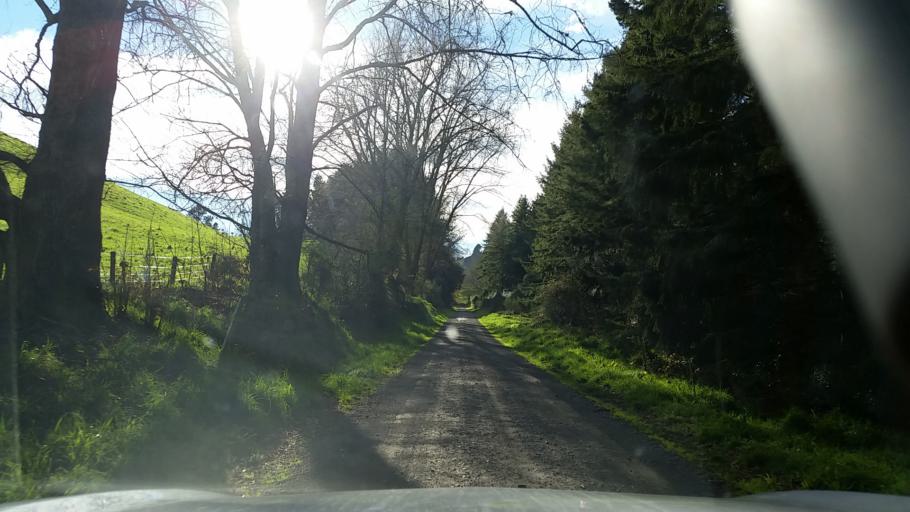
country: NZ
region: Waikato
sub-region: South Waikato District
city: Tokoroa
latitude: -38.3819
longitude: 176.0826
